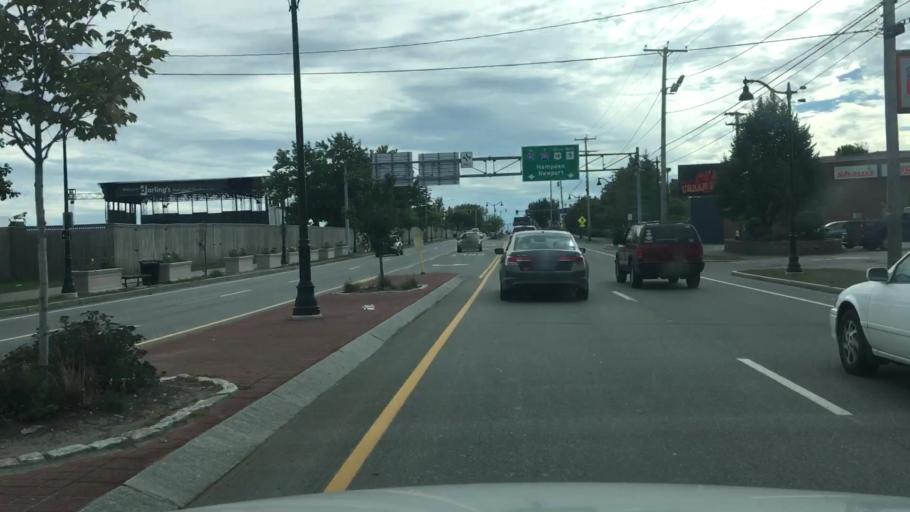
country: US
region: Maine
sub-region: Penobscot County
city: Bangor
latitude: 44.7950
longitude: -68.7746
